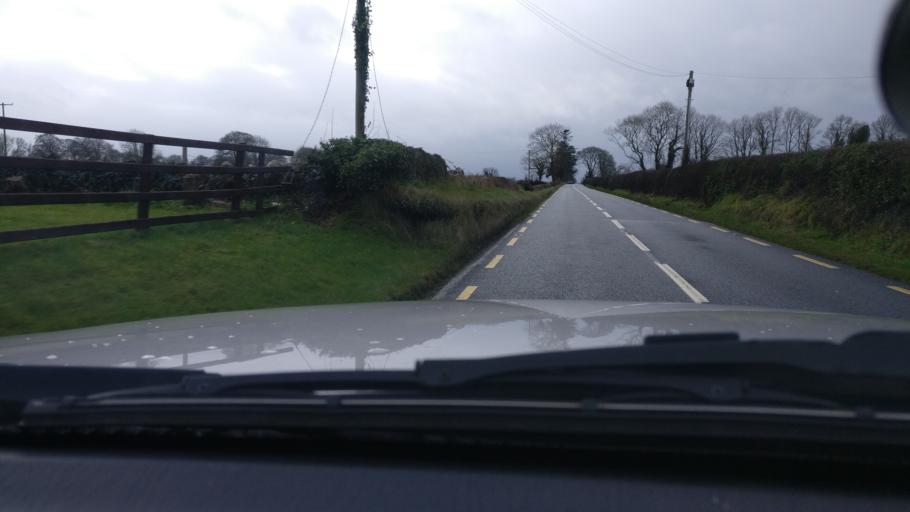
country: IE
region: Leinster
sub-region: An Longfort
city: Ballymahon
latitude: 53.5466
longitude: -7.7808
